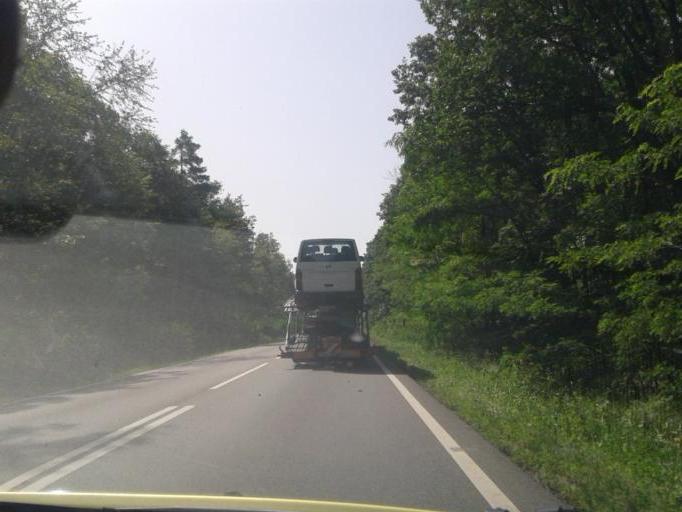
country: RO
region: Arges
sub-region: Comuna Cotmeana
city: Cotmeana
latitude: 44.9945
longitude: 24.6321
